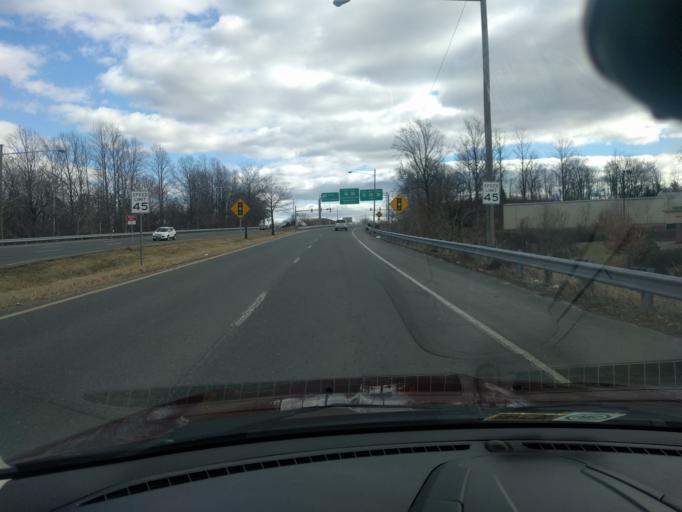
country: US
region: Virginia
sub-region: City of Lynchburg
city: Lynchburg
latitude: 37.3800
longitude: -79.1332
